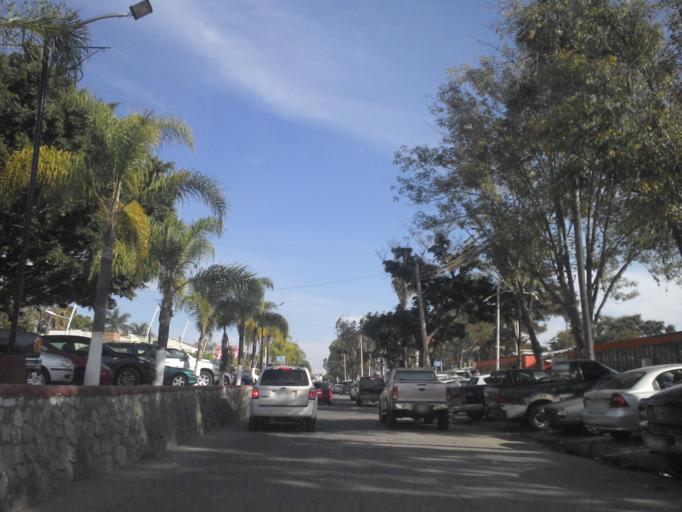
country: MX
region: Jalisco
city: Chapala
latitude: 20.2878
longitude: -103.1922
